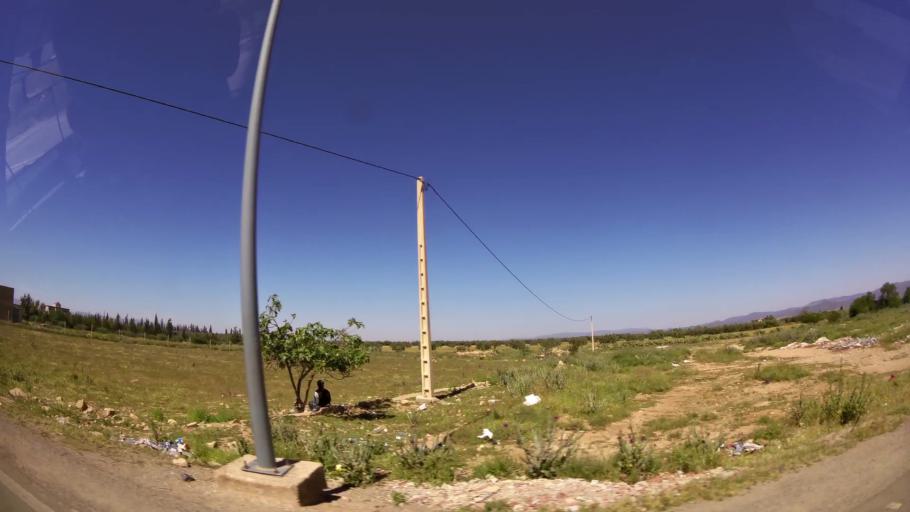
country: MA
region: Oriental
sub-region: Oujda-Angad
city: Oujda
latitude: 34.7043
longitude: -1.8572
